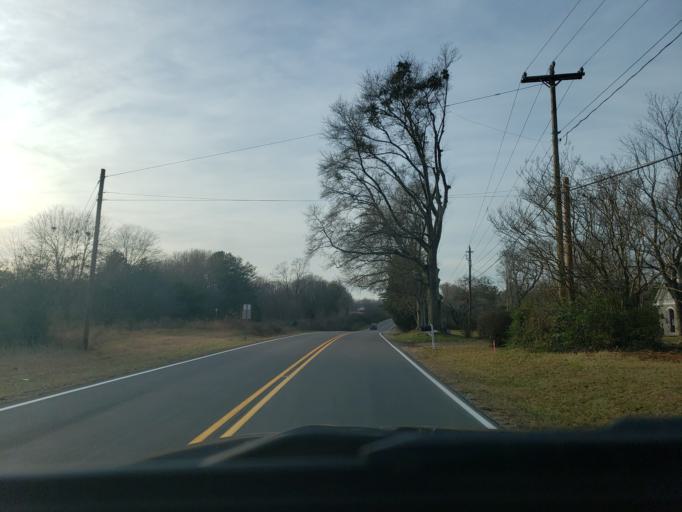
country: US
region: North Carolina
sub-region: Cleveland County
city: Boiling Springs
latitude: 35.3053
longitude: -81.7251
